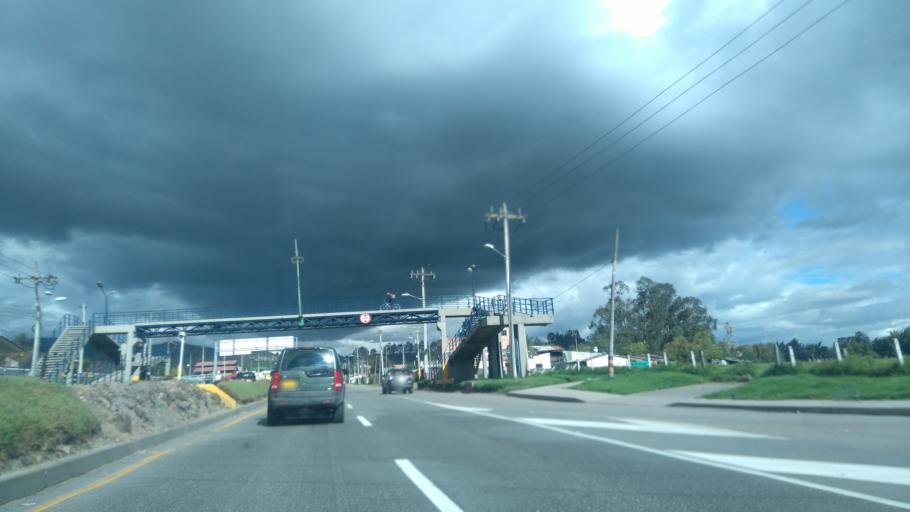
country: CO
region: Cundinamarca
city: El Rosal
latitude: 4.8194
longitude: -74.2292
